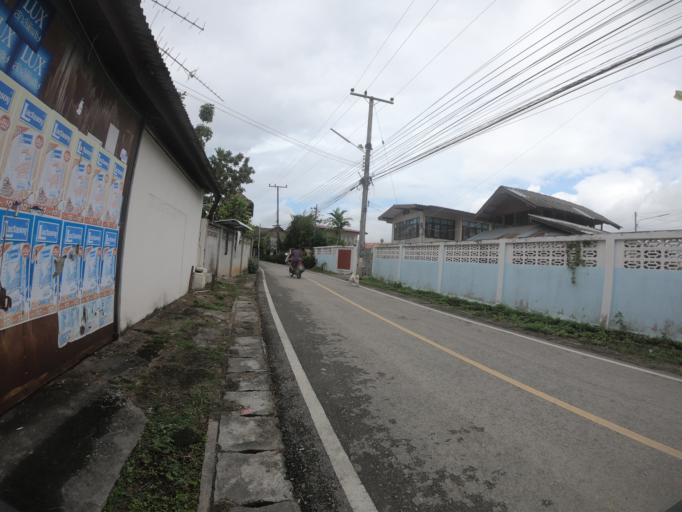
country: TH
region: Chiang Mai
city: Hang Dong
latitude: 18.7091
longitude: 98.9540
